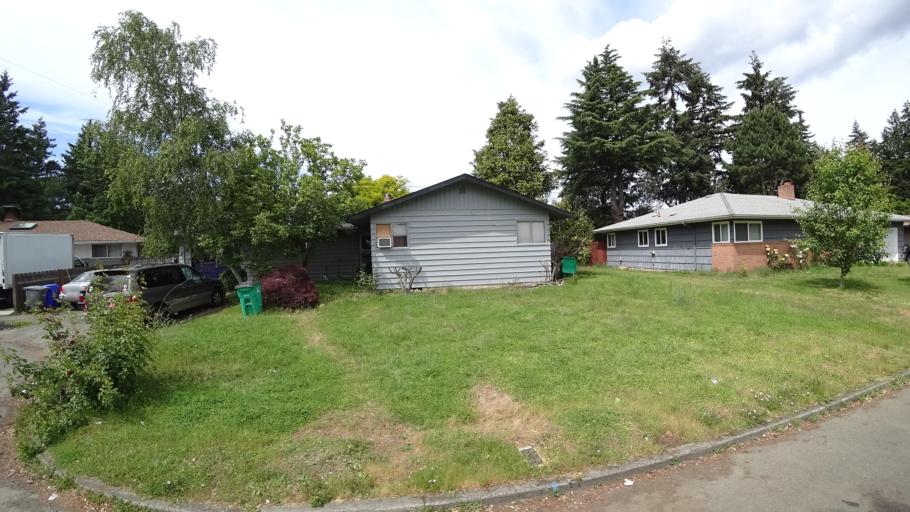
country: US
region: Oregon
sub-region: Multnomah County
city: Lents
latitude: 45.4883
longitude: -122.5501
